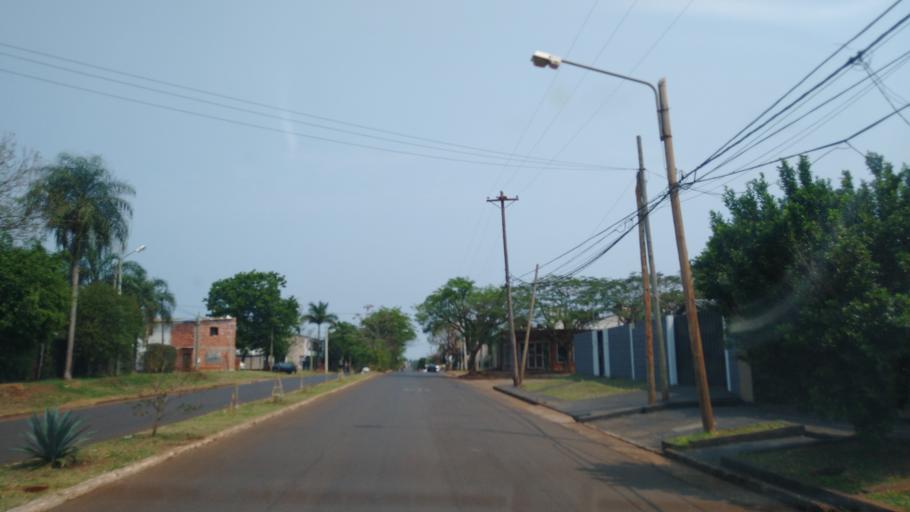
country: AR
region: Misiones
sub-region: Departamento de Capital
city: Posadas
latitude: -27.3861
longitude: -55.9306
